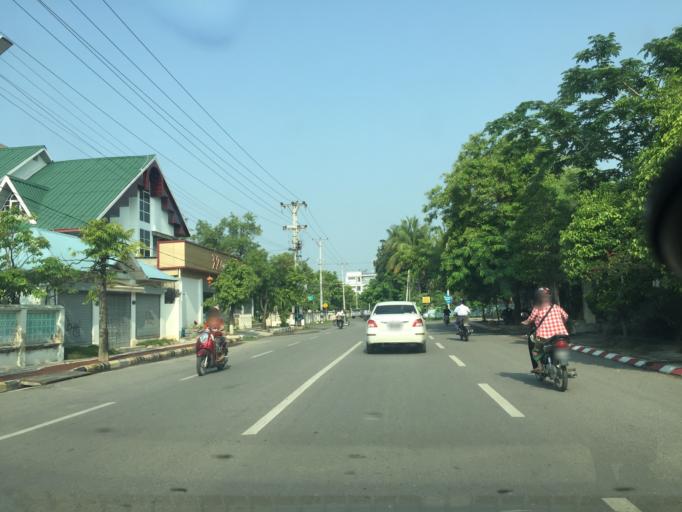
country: MM
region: Mandalay
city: Mandalay
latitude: 21.9730
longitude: 96.1008
